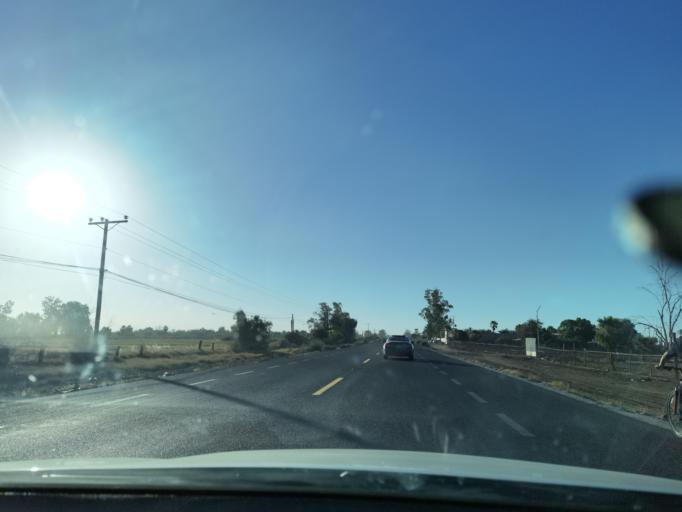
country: MX
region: Baja California
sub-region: Mexicali
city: Islas Agrarias Grupo A
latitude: 32.6469
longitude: -115.3260
